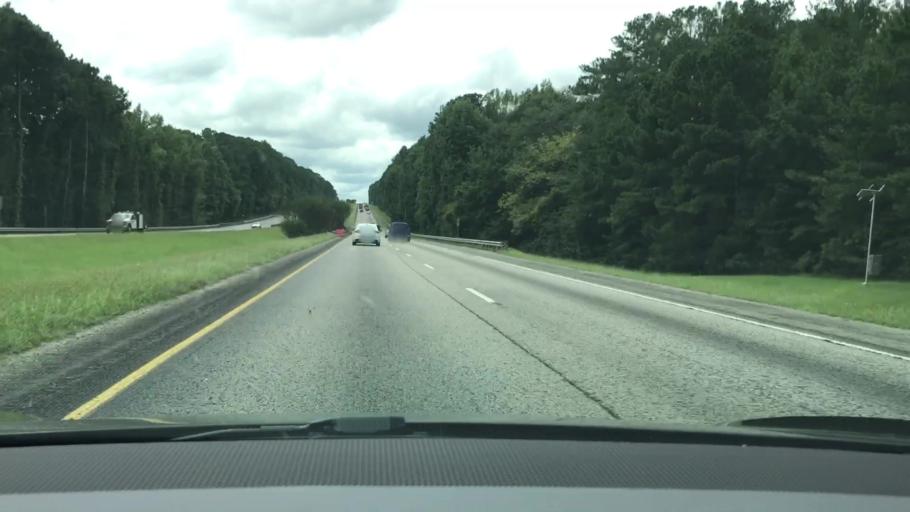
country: US
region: Georgia
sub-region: Troup County
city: La Grange
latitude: 32.9688
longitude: -85.0736
